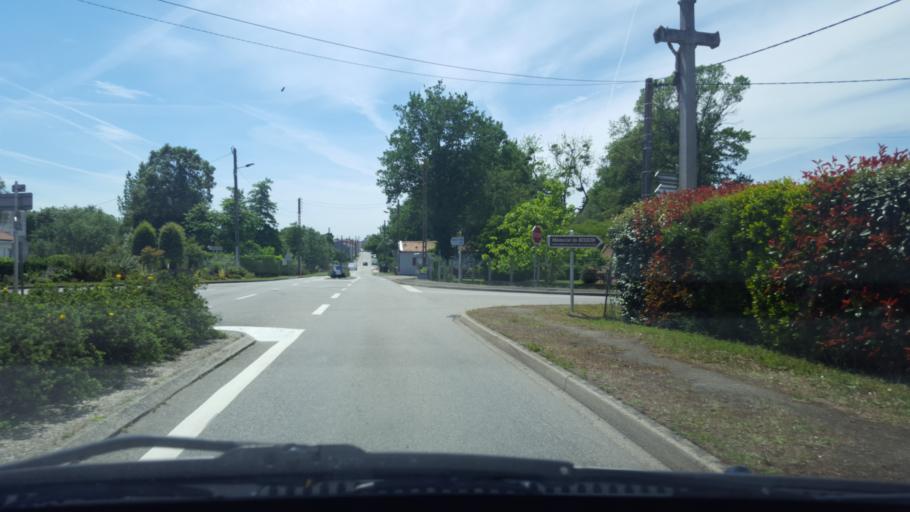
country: FR
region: Pays de la Loire
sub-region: Departement de la Loire-Atlantique
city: La Limouziniere
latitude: 47.0180
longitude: -1.5664
